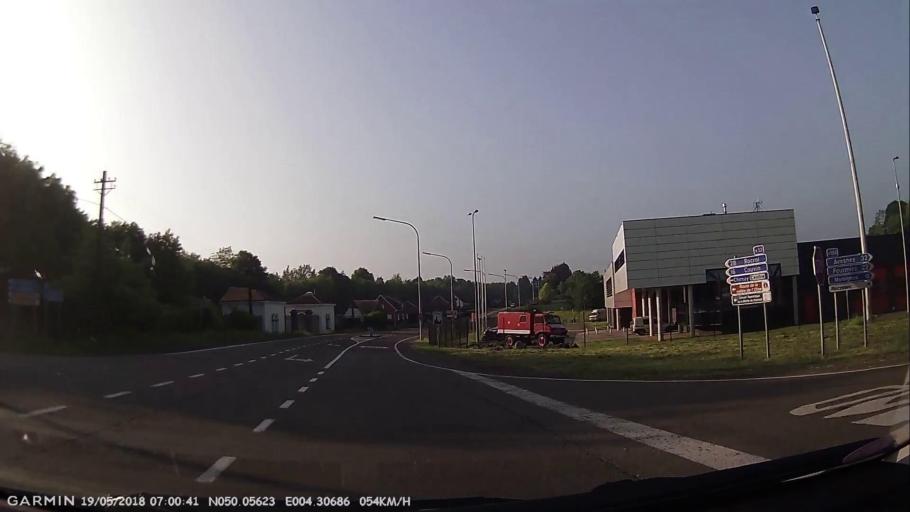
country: BE
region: Wallonia
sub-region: Province du Hainaut
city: Chimay
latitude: 50.0561
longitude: 4.3070
